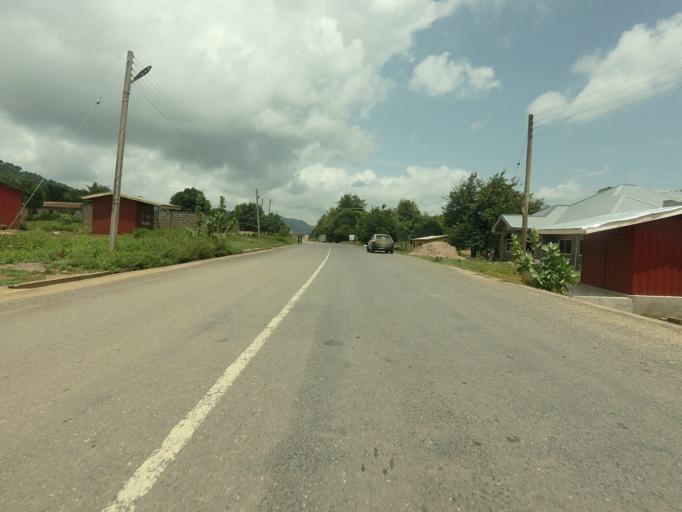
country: GH
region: Volta
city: Ho
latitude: 6.7093
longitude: 0.3348
